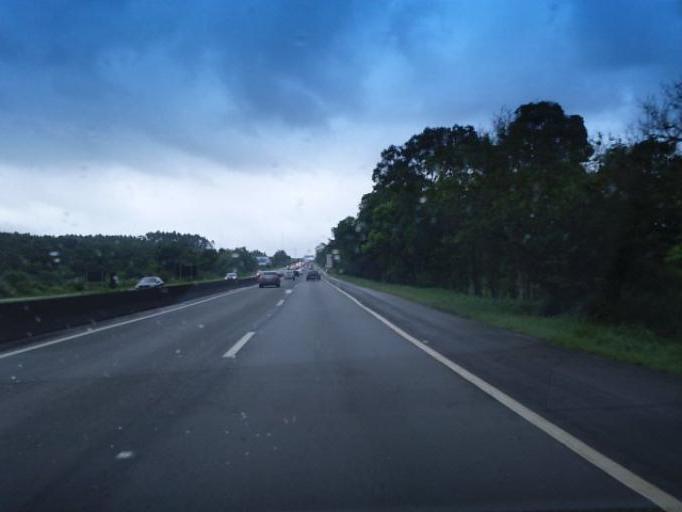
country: BR
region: Santa Catarina
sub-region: Barra Velha
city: Barra Velha
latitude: -26.6173
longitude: -48.7188
